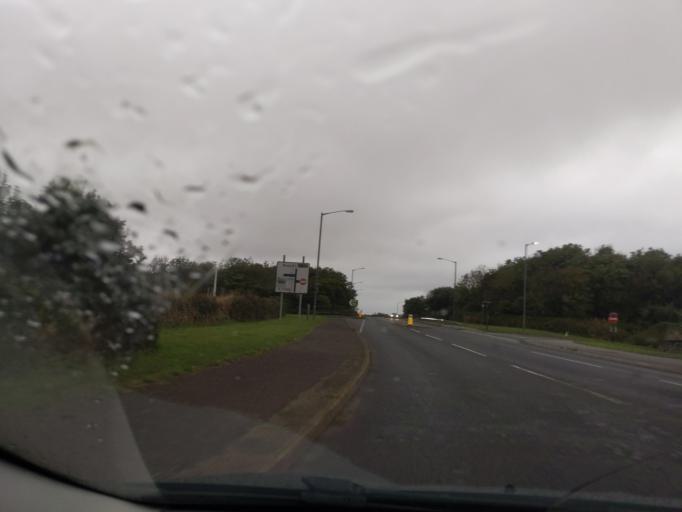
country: GB
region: England
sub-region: Cornwall
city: Camborne
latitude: 50.2162
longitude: -5.3189
